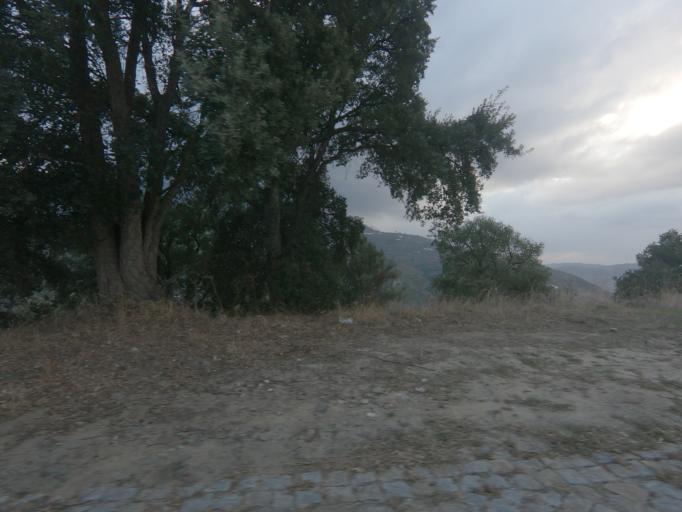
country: PT
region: Vila Real
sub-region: Mesao Frio
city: Mesao Frio
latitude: 41.1615
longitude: -7.8515
